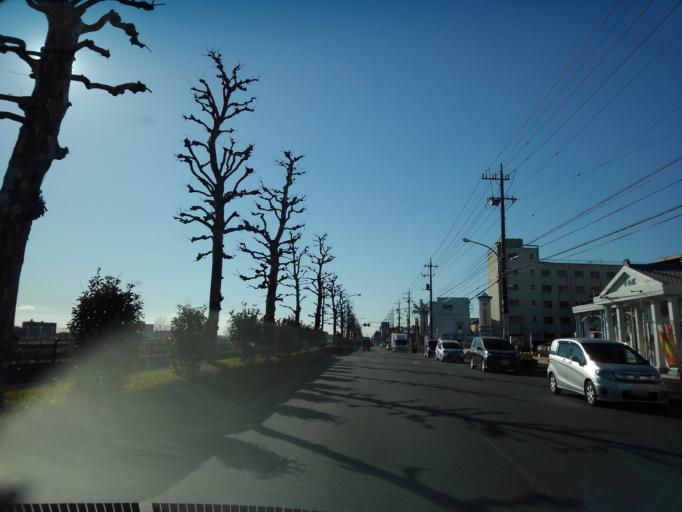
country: JP
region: Tokyo
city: Fussa
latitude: 35.7414
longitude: 139.3829
